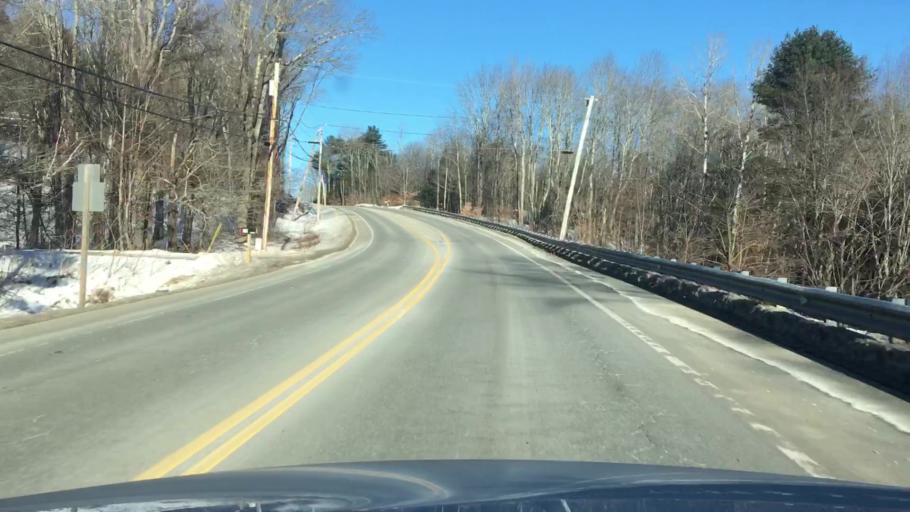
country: US
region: Maine
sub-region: Cumberland County
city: Freeport
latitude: 43.8771
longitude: -70.1074
